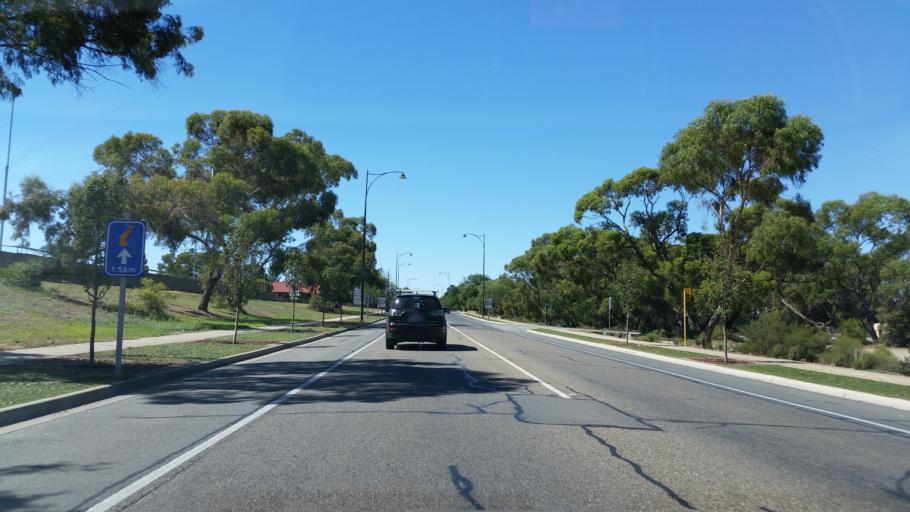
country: AU
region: South Australia
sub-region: Murray Bridge
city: Murray Bridge
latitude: -35.1249
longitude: 139.2616
